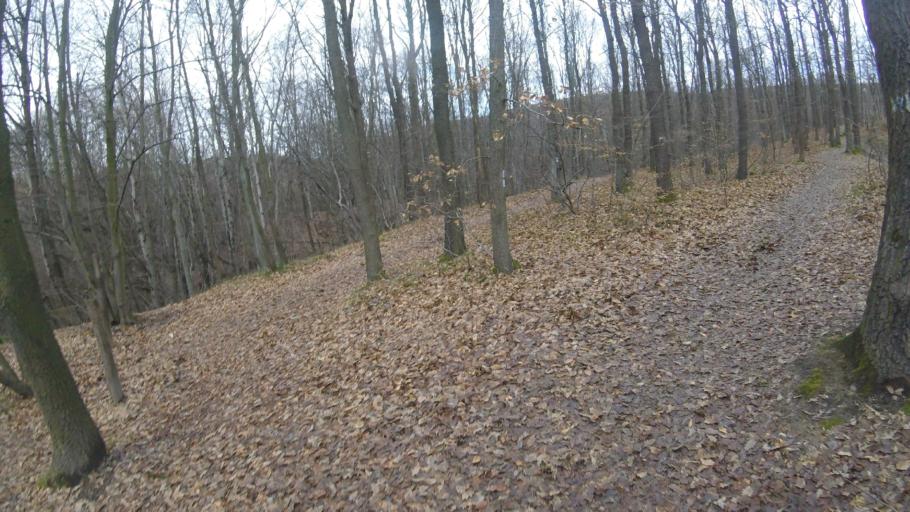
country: HU
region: Pest
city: Pilisszentkereszt
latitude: 47.6904
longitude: 18.9124
